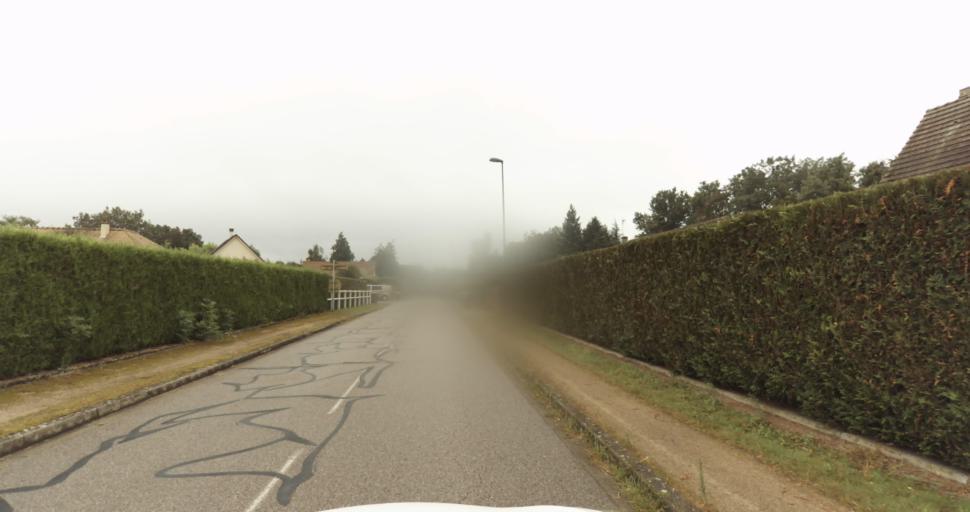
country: FR
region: Haute-Normandie
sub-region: Departement de l'Eure
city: Normanville
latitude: 49.0996
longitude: 1.1449
